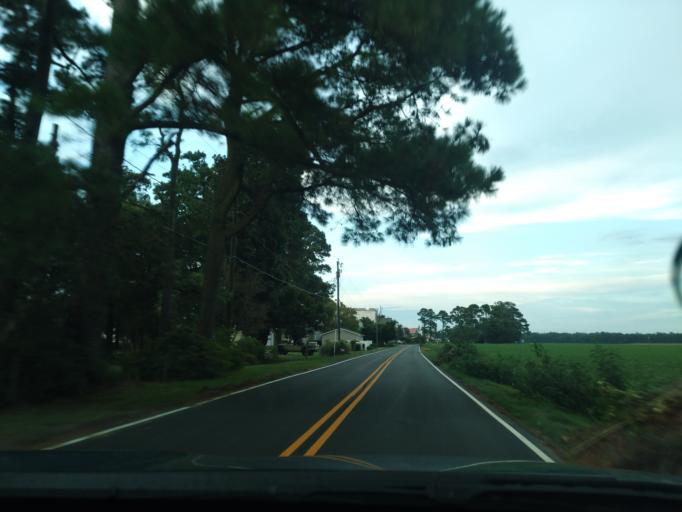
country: US
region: North Carolina
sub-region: Chowan County
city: Edenton
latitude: 35.9356
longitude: -76.6389
